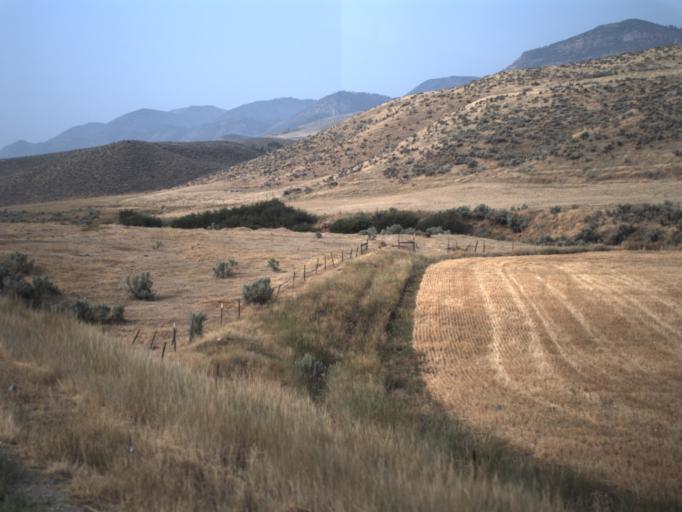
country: US
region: Utah
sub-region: Summit County
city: Coalville
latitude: 41.0079
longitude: -111.5177
